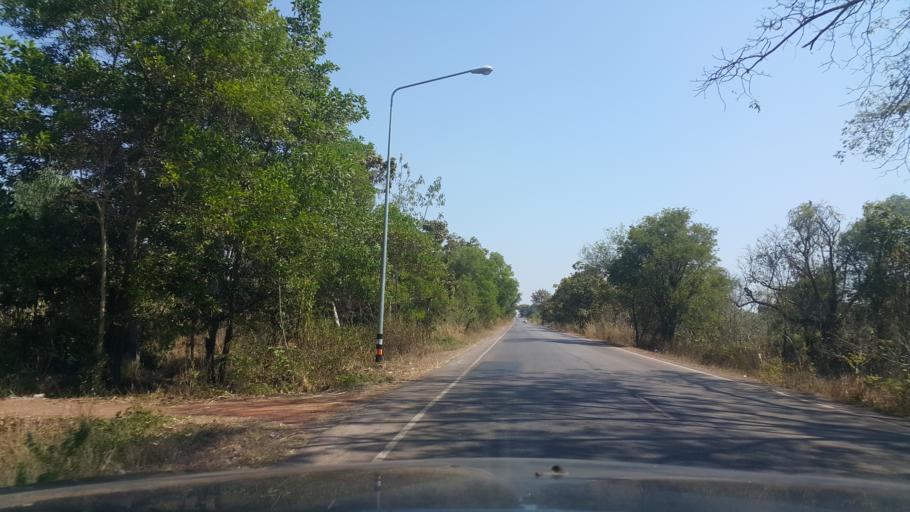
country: TH
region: Changwat Udon Thani
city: Ban Dung
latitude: 17.6083
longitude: 103.2544
